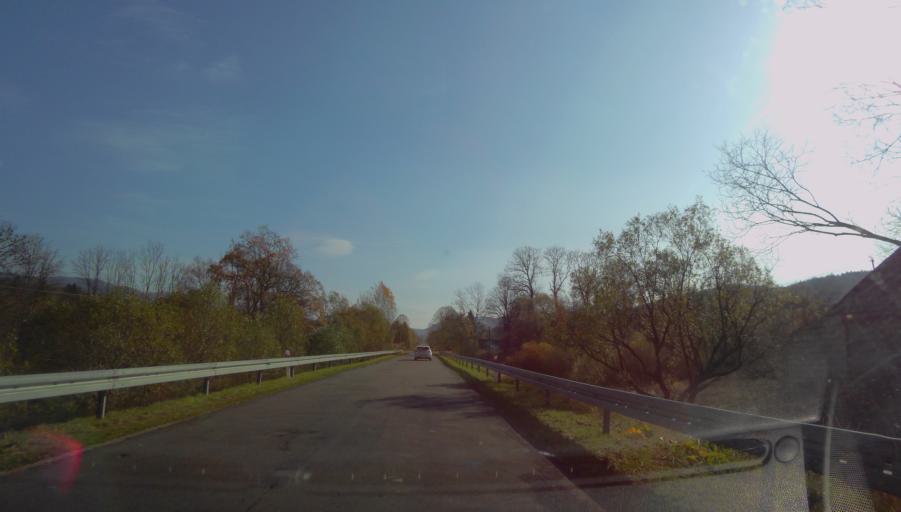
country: PL
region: Subcarpathian Voivodeship
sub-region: Powiat sanocki
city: Komancza
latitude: 49.2319
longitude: 22.1573
